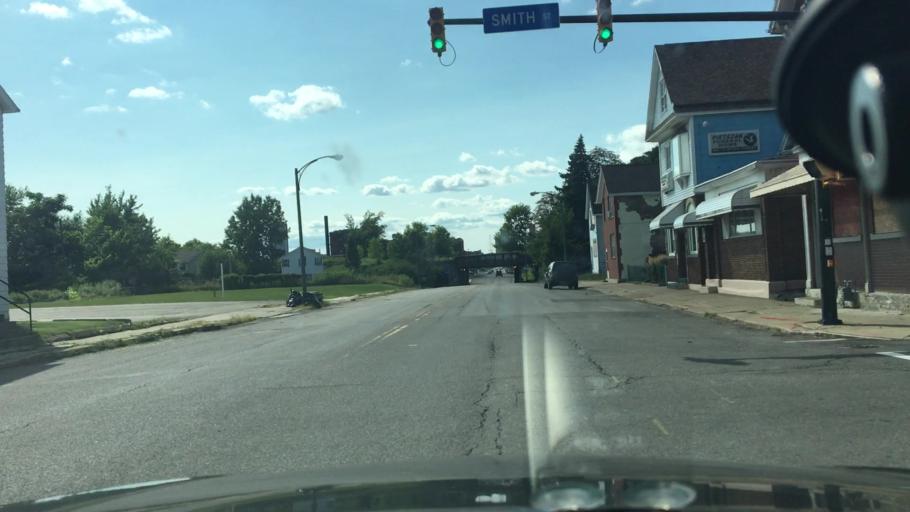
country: US
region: New York
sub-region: Erie County
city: Buffalo
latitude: 42.8802
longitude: -78.8441
